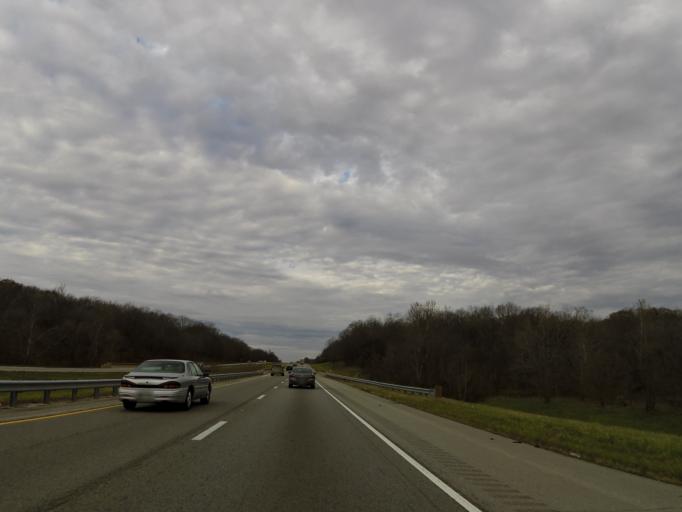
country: US
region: Illinois
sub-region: Clinton County
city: Wamac
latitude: 38.3802
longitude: -89.1121
